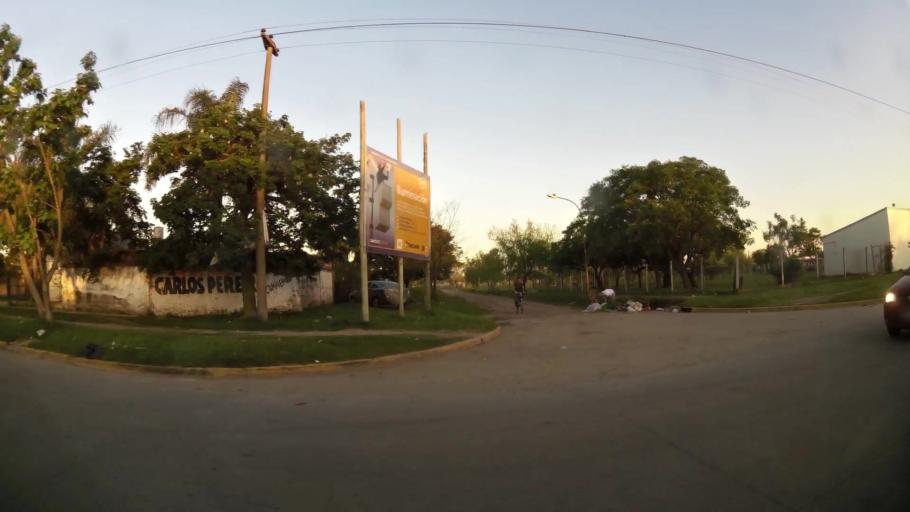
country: AR
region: Santa Fe
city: Santa Fe de la Vera Cruz
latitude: -31.5918
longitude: -60.6987
